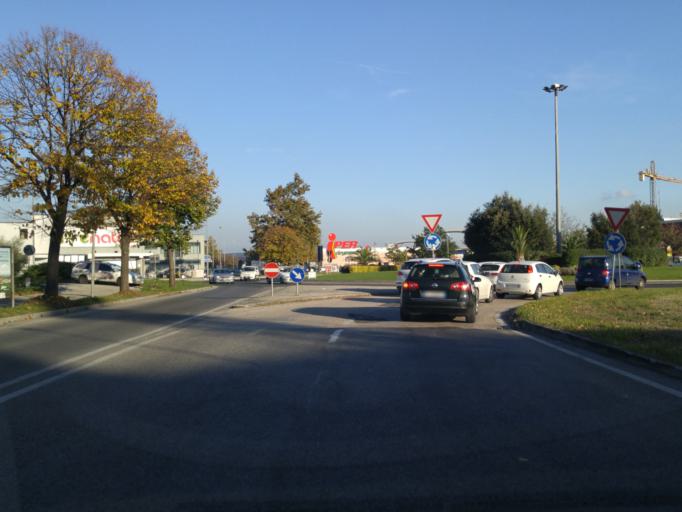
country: IT
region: The Marches
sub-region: Provincia di Pesaro e Urbino
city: Pesaro
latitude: 43.9060
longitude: 12.8647
